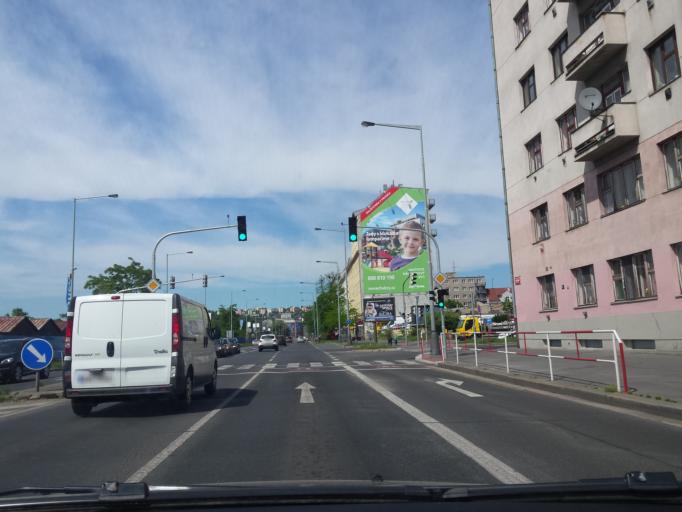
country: CZ
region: Praha
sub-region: Praha 8
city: Karlin
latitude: 50.1026
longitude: 14.4434
